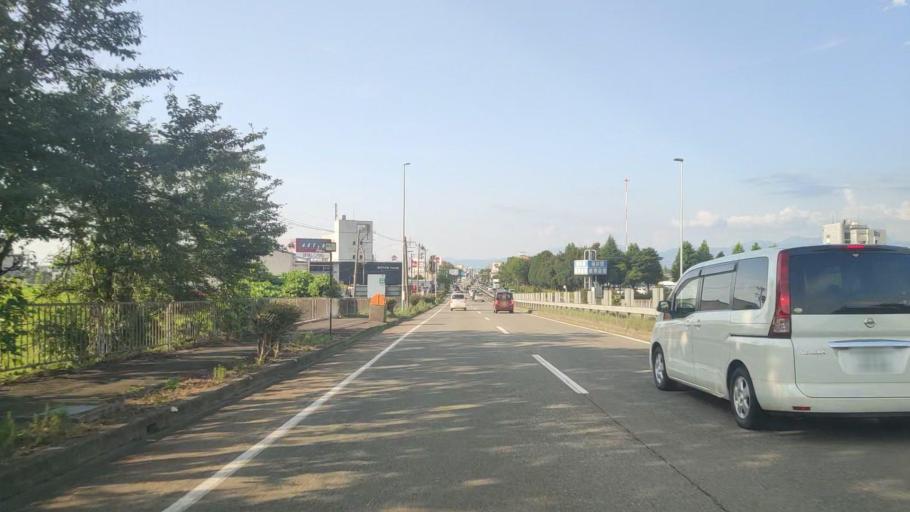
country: JP
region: Fukui
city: Fukui-shi
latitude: 36.0356
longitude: 136.2283
